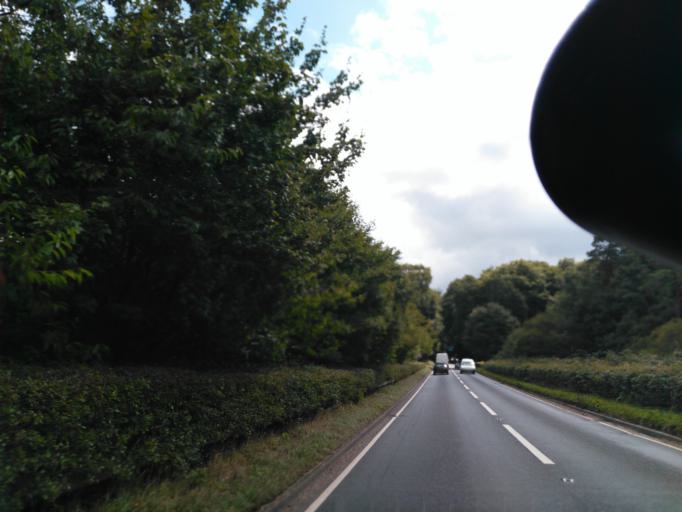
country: GB
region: England
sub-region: Dorset
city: Lytchett Matravers
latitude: 50.7557
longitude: -2.0487
